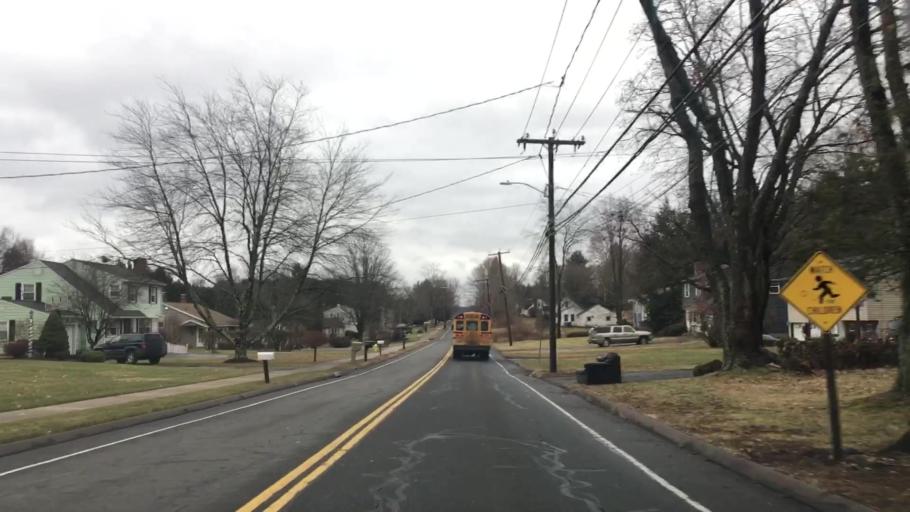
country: US
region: Connecticut
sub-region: Tolland County
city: Rockville
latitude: 41.8628
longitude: -72.4932
